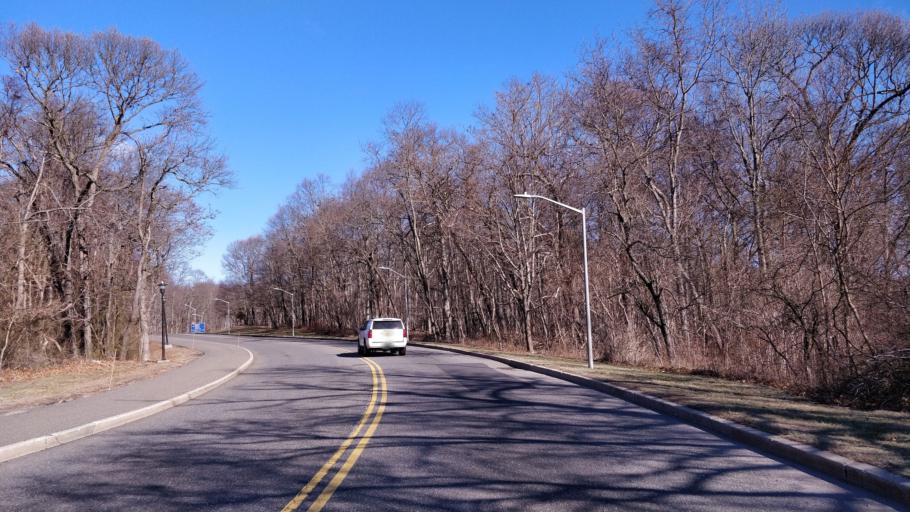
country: US
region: New York
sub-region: Suffolk County
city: Stony Brook
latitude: 40.8993
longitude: -73.1238
